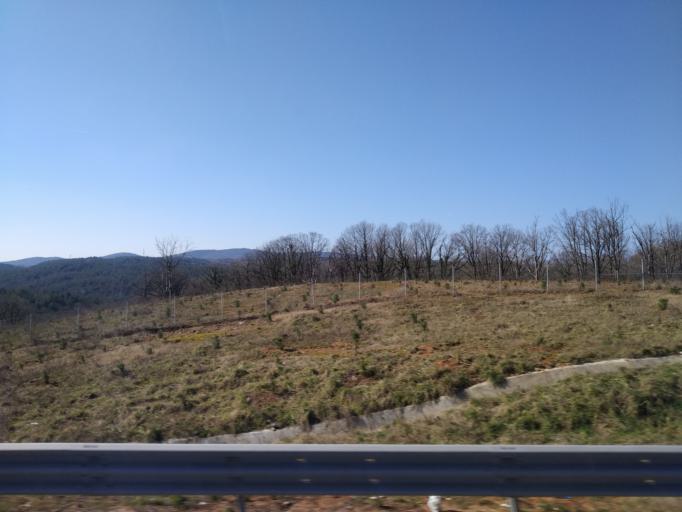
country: TR
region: Istanbul
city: Sancaktepe
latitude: 41.0685
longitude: 29.2755
